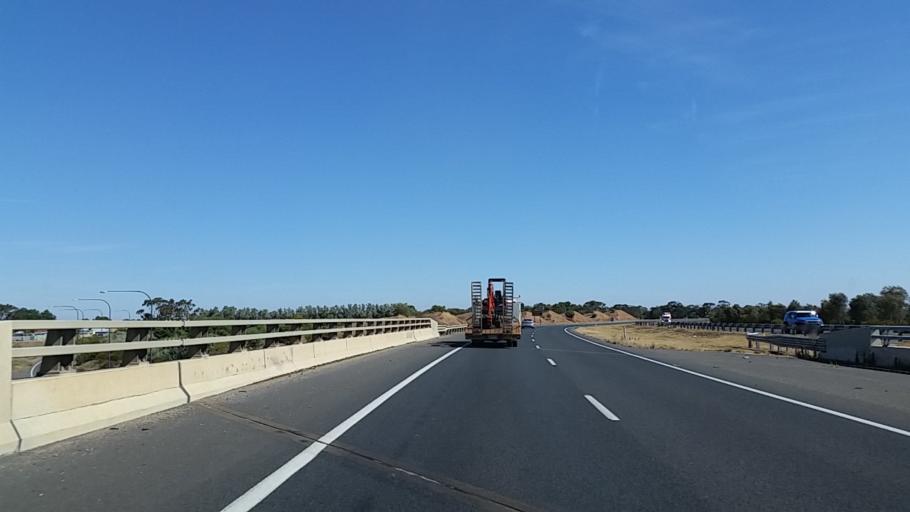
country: AU
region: South Australia
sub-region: Gawler
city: Gawler
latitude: -34.5996
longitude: 138.7263
